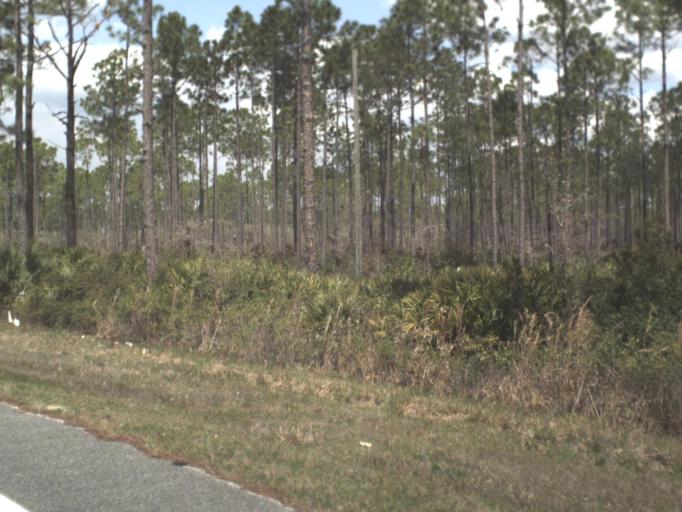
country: US
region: Florida
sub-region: Franklin County
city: Eastpoint
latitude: 29.8101
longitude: -84.8409
